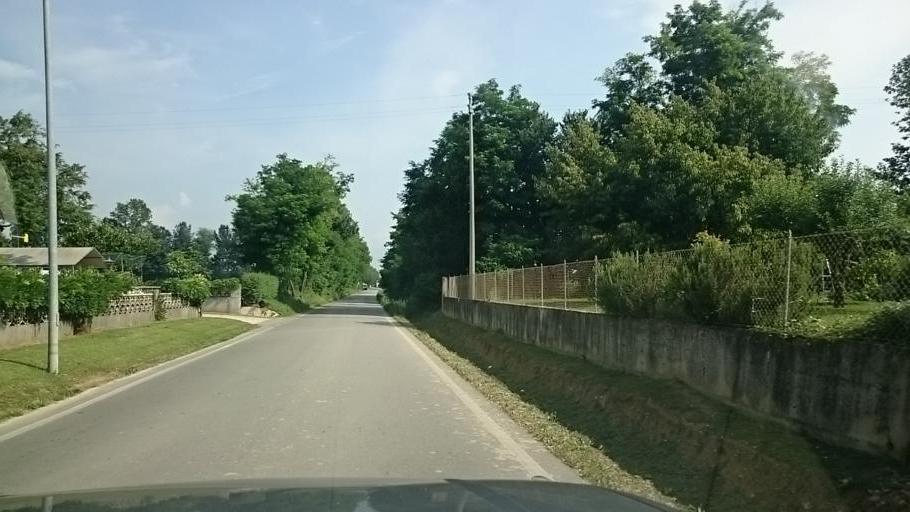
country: IT
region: Veneto
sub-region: Provincia di Treviso
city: Sant'Andrea
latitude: 45.6681
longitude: 11.8851
